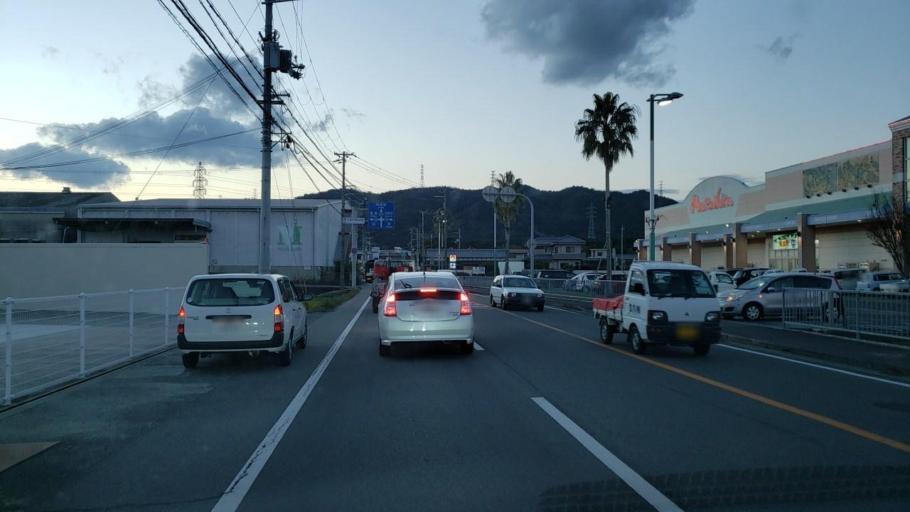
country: JP
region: Hyogo
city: Fukura
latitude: 34.3023
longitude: 134.7456
